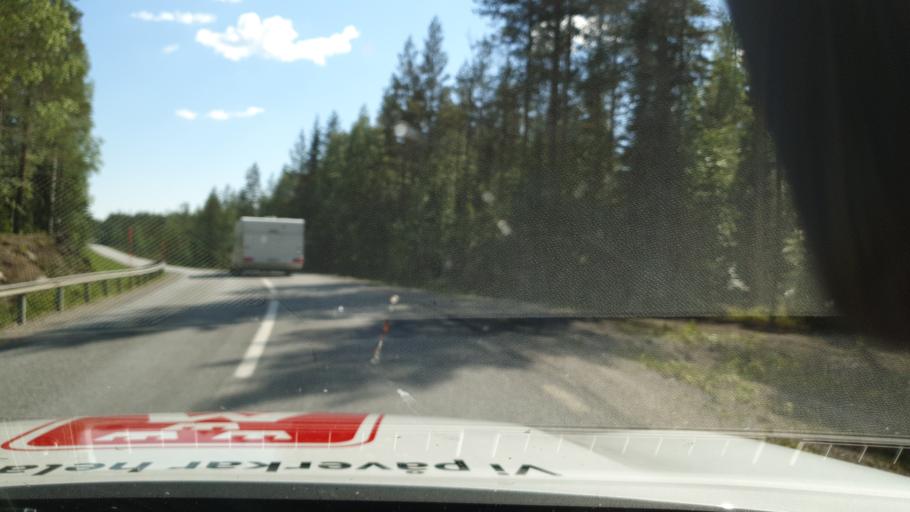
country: SE
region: Vaesterbotten
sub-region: Skelleftea Kommun
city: Burtraesk
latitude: 64.3462
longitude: 20.2336
